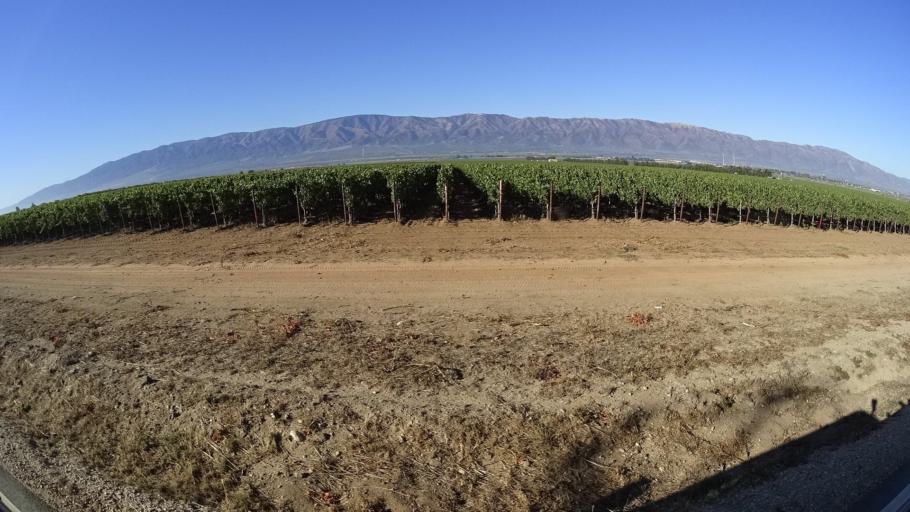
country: US
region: California
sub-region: Monterey County
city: Gonzales
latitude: 36.5101
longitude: -121.4058
